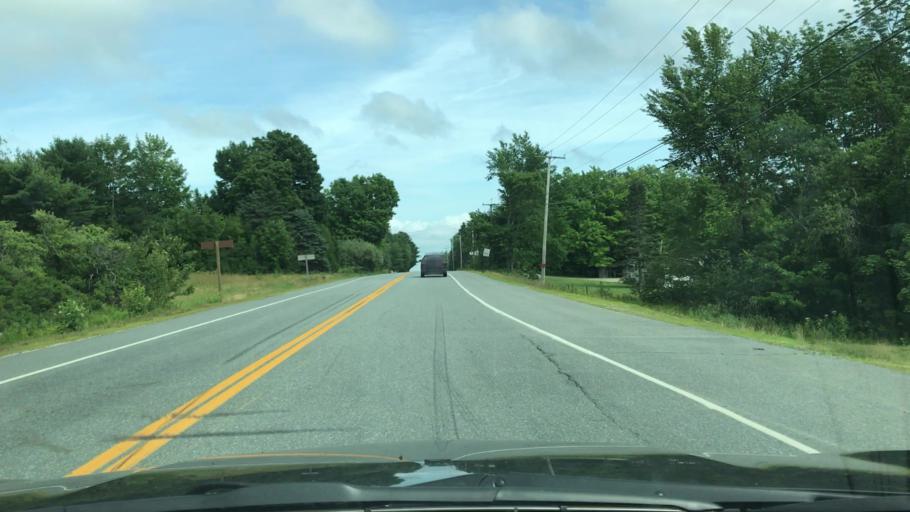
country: US
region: Maine
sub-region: Hancock County
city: Surry
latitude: 44.5448
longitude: -68.5164
